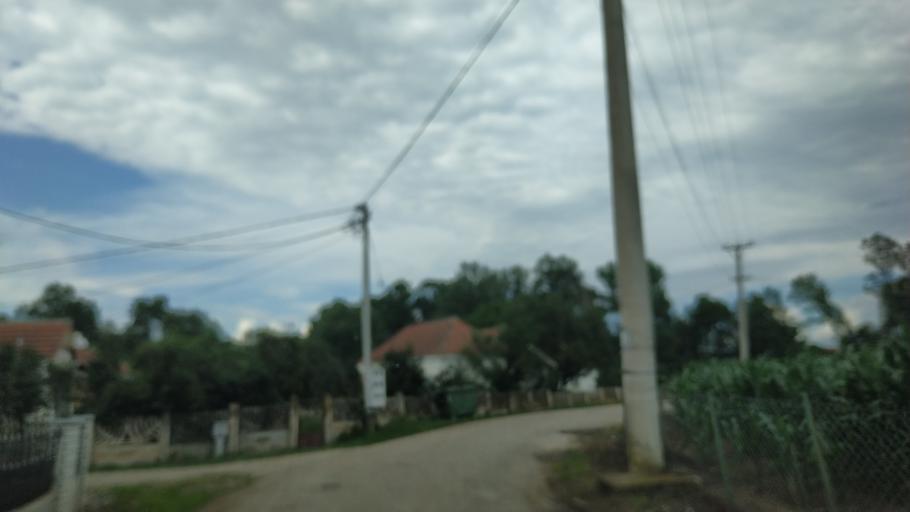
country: RS
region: Central Serbia
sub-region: Nisavski Okrug
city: Razanj
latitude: 43.5918
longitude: 21.6080
